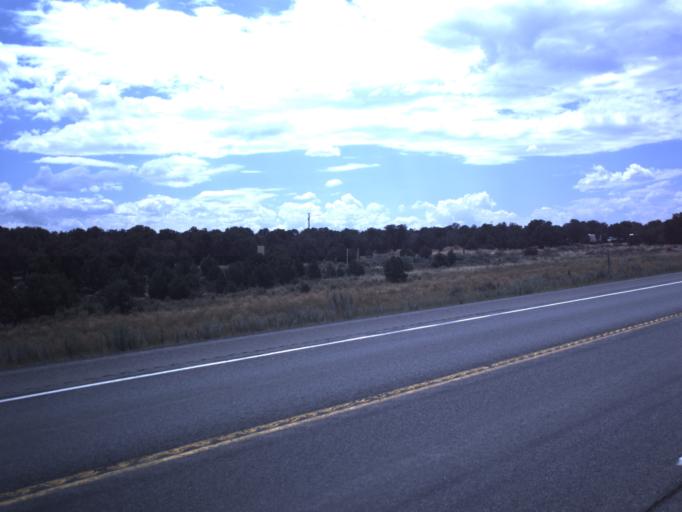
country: US
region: Utah
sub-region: Duchesne County
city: Duchesne
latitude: 40.1713
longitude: -110.5667
